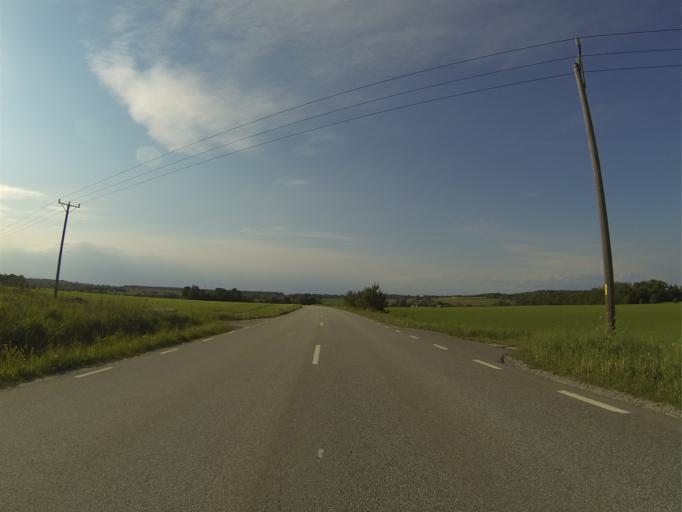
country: SE
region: Skane
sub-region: Lunds Kommun
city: Lund
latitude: 55.7059
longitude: 13.3023
